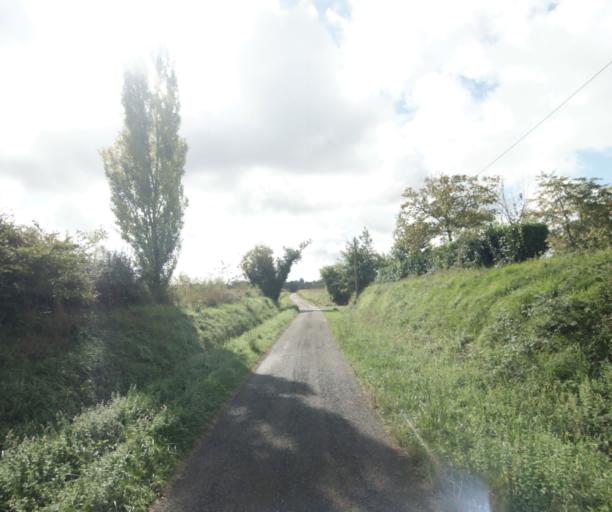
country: FR
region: Midi-Pyrenees
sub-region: Departement du Gers
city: Nogaro
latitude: 43.8334
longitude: -0.0928
